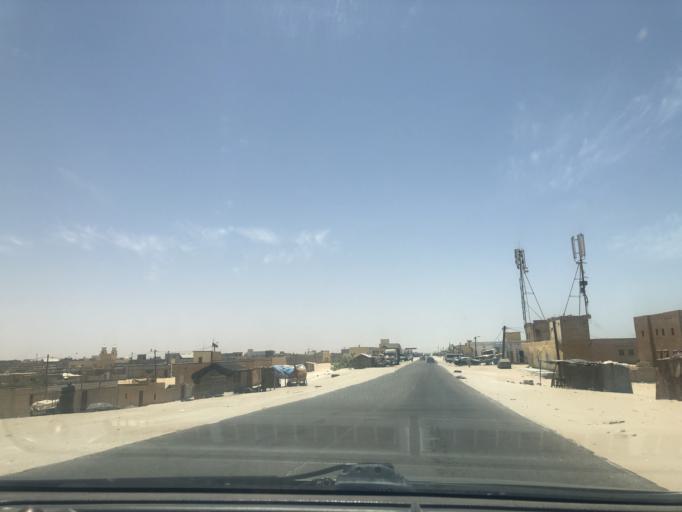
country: MR
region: Nouakchott
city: Nouakchott
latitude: 18.0183
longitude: -15.9587
